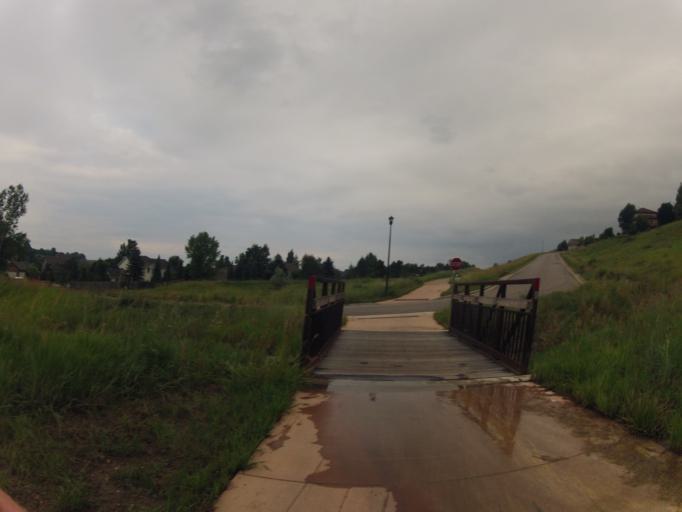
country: US
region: Colorado
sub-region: Larimer County
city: Fort Collins
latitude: 40.5276
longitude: -105.1253
